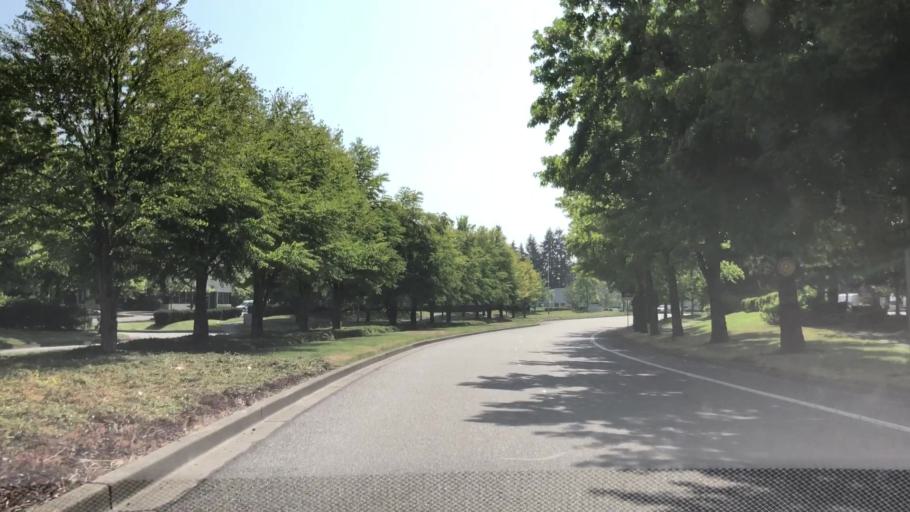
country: US
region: Washington
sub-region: Thurston County
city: Tanglewilde-Thompson Place
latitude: 47.0707
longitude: -122.7574
